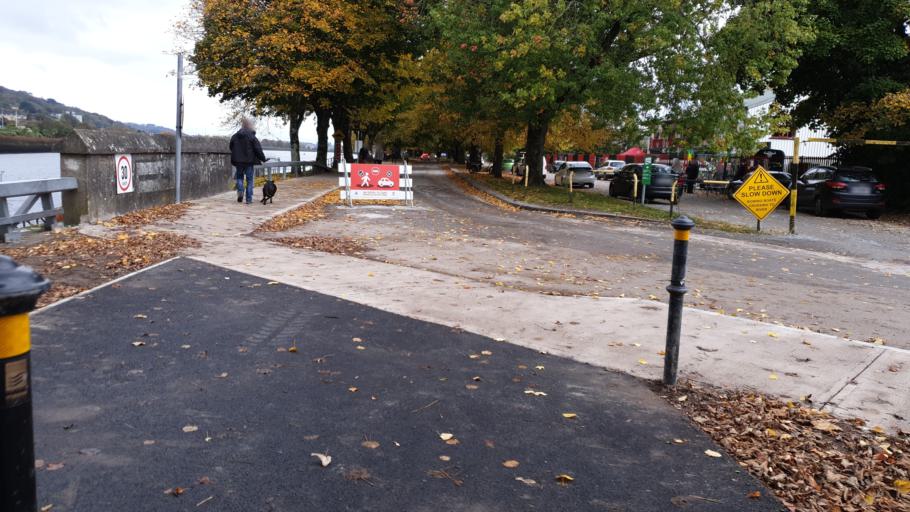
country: IE
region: Munster
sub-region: County Cork
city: Cork
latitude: 51.9013
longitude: -8.4383
